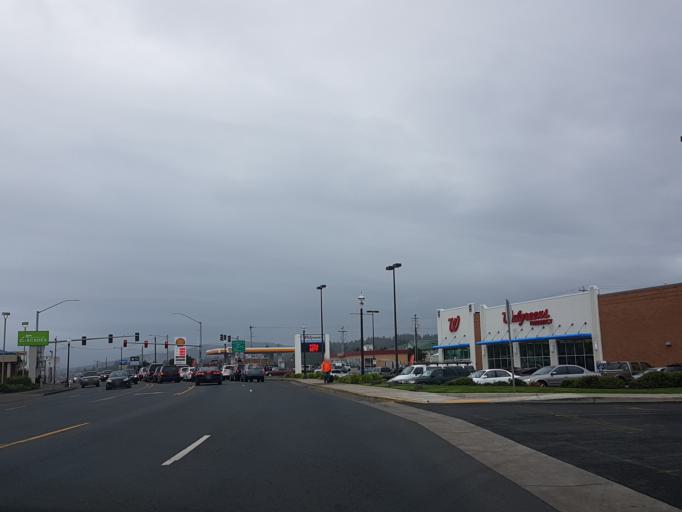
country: US
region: Oregon
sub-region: Lincoln County
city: Newport
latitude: 44.6354
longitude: -124.0533
